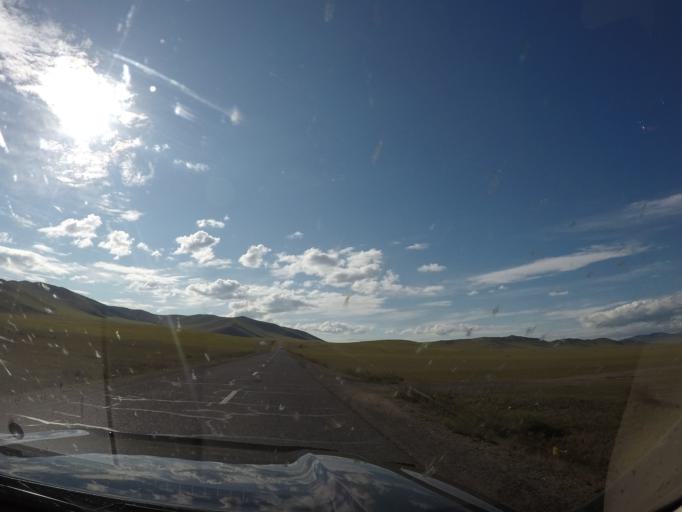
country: MN
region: Hentiy
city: Modot
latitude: 47.7444
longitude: 108.9886
